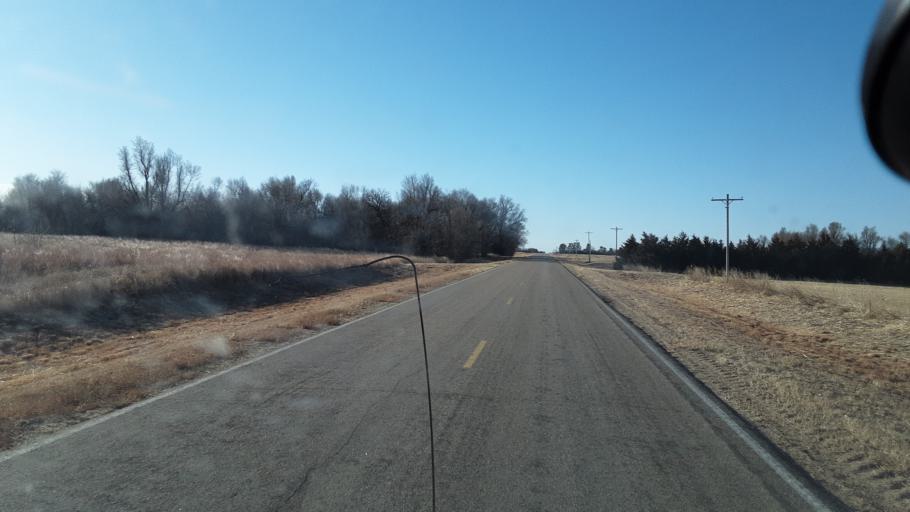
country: US
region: Kansas
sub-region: Barton County
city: Ellinwood
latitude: 38.3277
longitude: -98.6647
